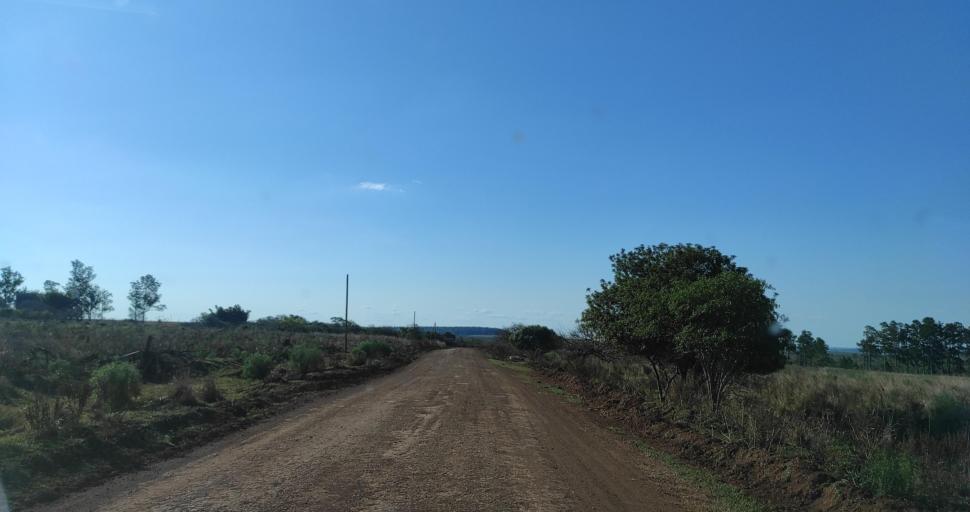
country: PY
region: Itapua
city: San Juan del Parana
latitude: -27.4409
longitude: -56.0613
